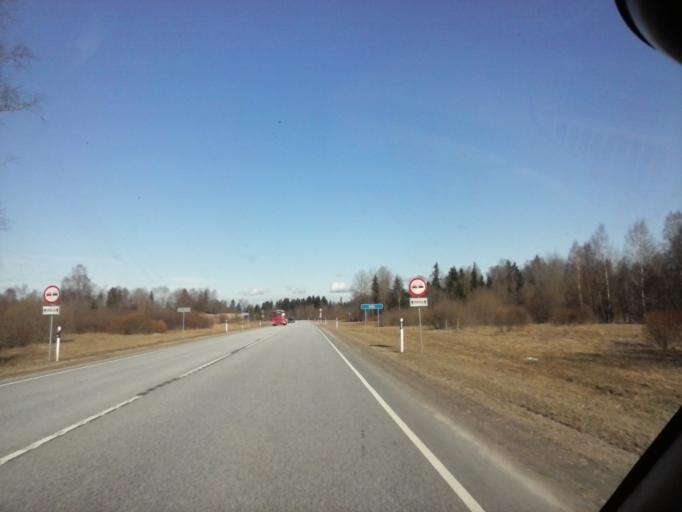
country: EE
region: Harju
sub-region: Anija vald
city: Kehra
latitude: 59.1608
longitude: 25.2855
